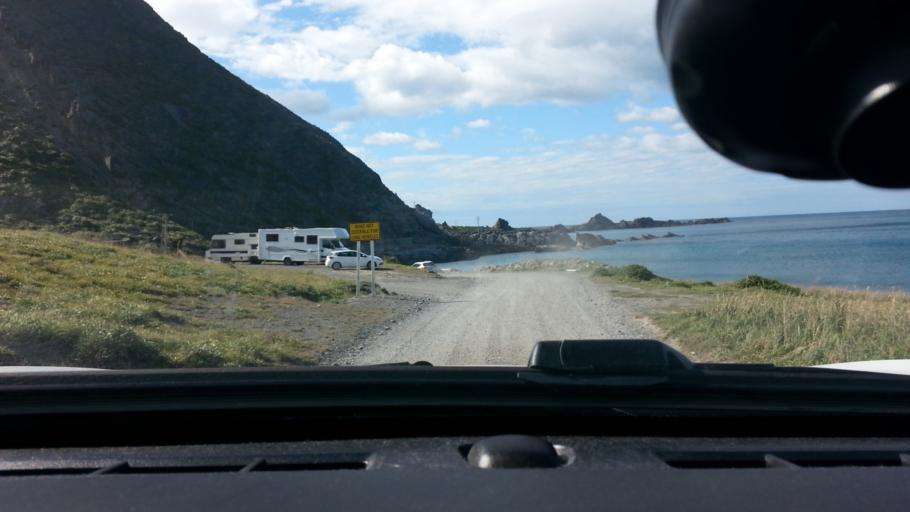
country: NZ
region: Wellington
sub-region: South Wairarapa District
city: Waipawa
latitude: -41.6044
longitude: 175.2624
